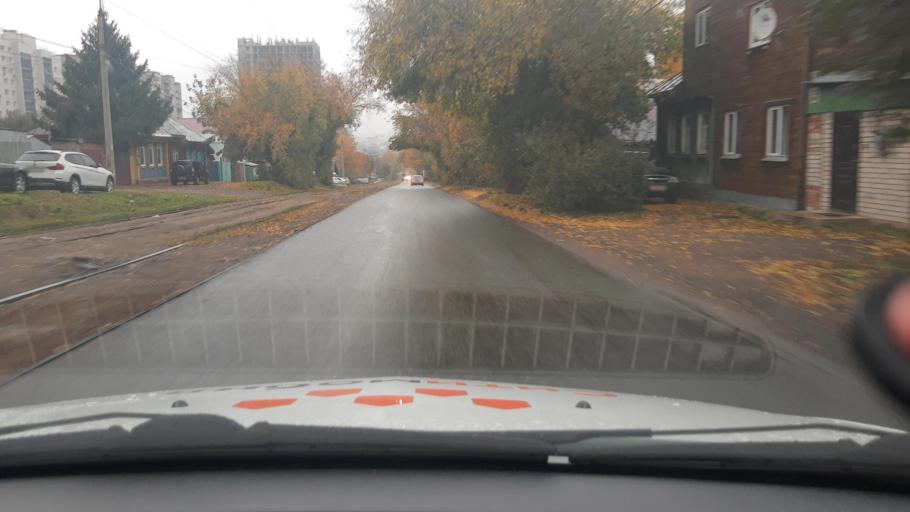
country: RU
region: Bashkortostan
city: Ufa
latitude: 54.7131
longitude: 55.9808
